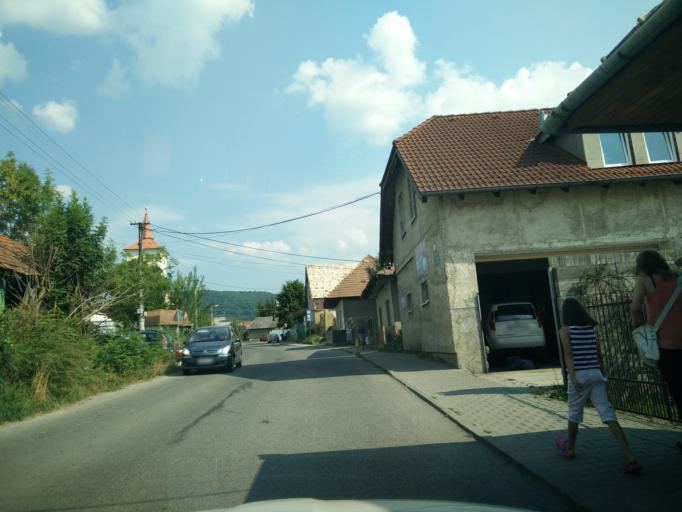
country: SK
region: Nitriansky
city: Prievidza
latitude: 48.7327
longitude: 18.6187
